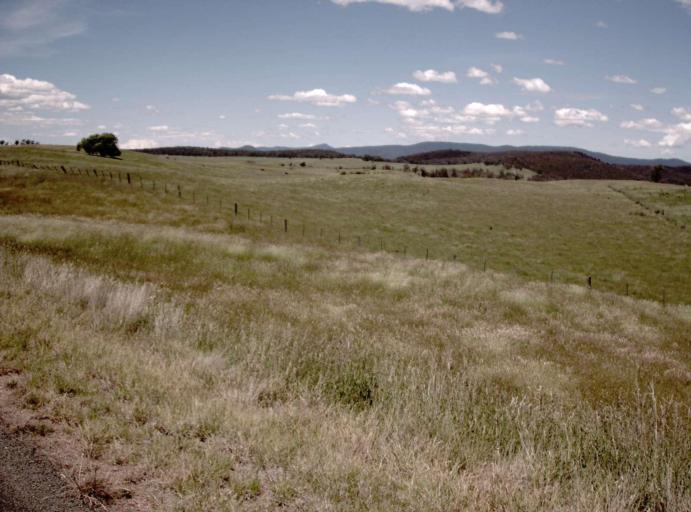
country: AU
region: New South Wales
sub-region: Snowy River
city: Jindabyne
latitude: -37.0988
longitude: 148.2547
